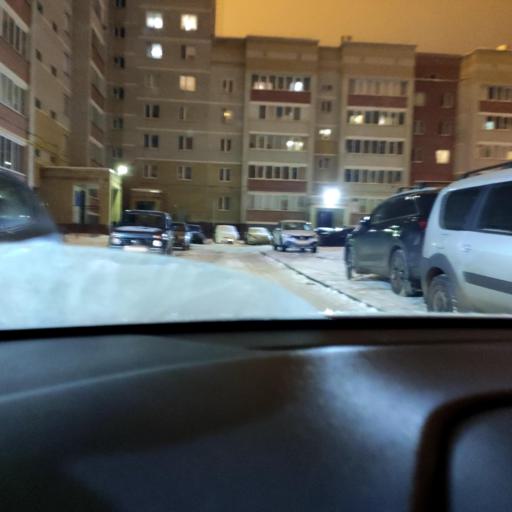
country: RU
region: Tatarstan
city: Osinovo
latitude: 55.8761
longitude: 48.8970
